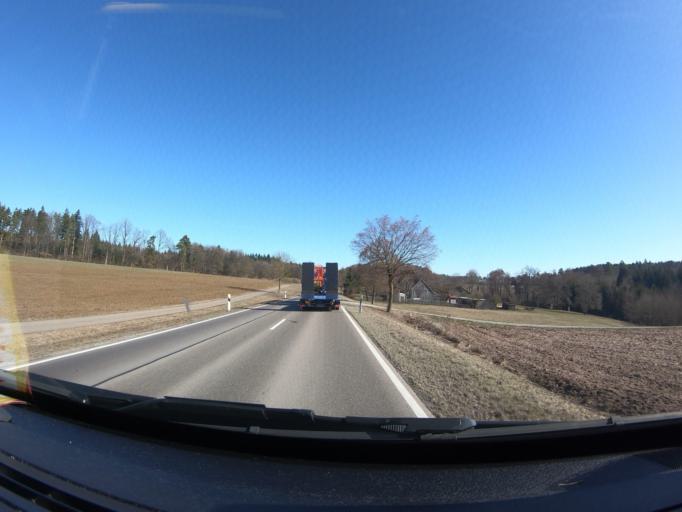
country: DE
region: Baden-Wuerttemberg
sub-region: Regierungsbezirk Stuttgart
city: Gaildorf
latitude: 49.0207
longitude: 9.8164
